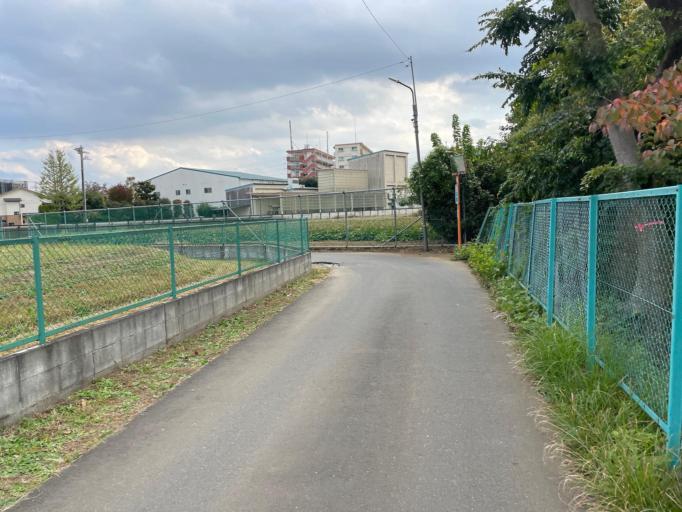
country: JP
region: Tokyo
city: Hino
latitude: 35.7304
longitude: 139.3876
